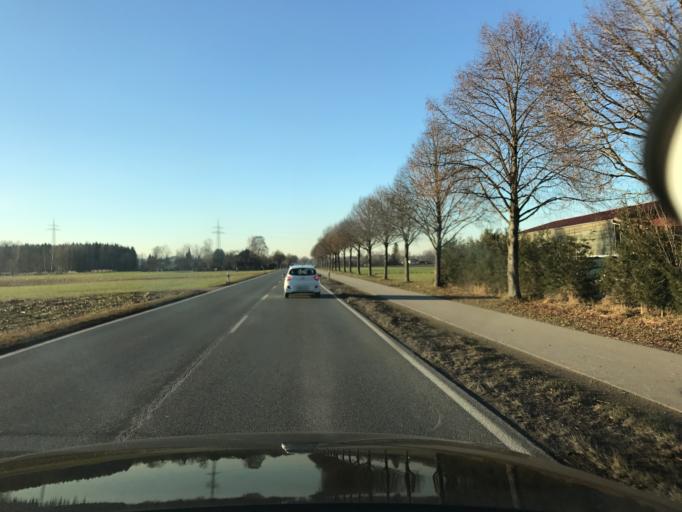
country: DE
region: Bavaria
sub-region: Upper Bavaria
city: Bad Aibling
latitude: 47.8425
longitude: 12.0323
